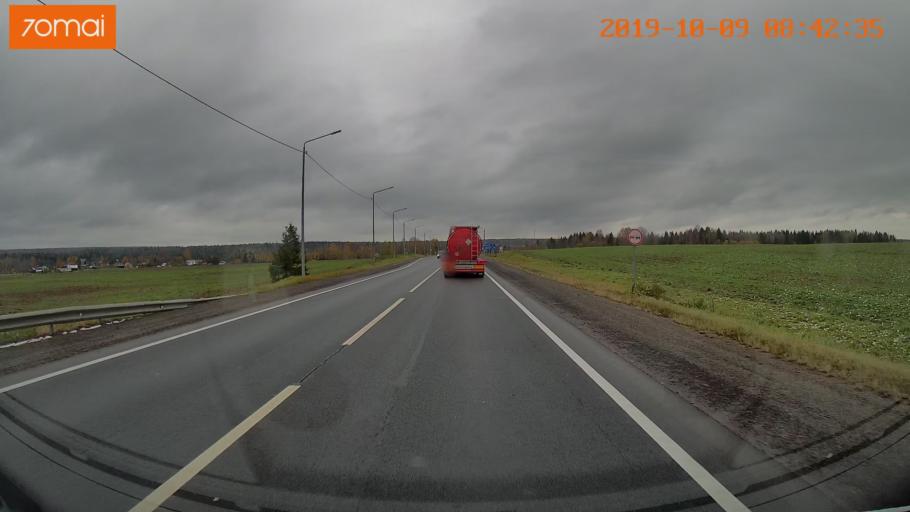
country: RU
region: Vologda
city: Gryazovets
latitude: 59.0172
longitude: 40.1178
